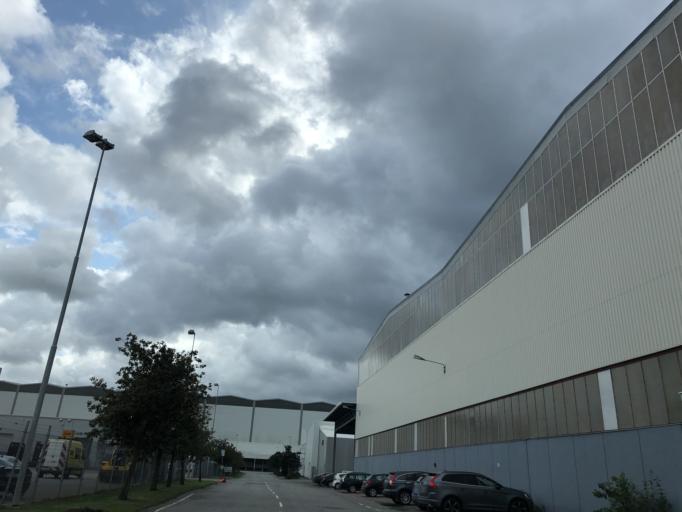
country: SE
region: Vaestra Goetaland
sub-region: Goteborg
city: Torslanda
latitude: 57.7000
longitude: 11.8210
